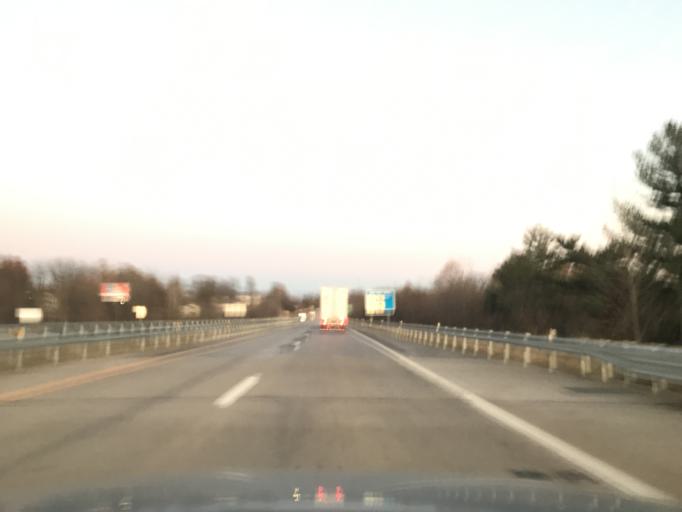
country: US
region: Missouri
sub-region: Marion County
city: Hannibal
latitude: 39.7145
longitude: -91.4003
